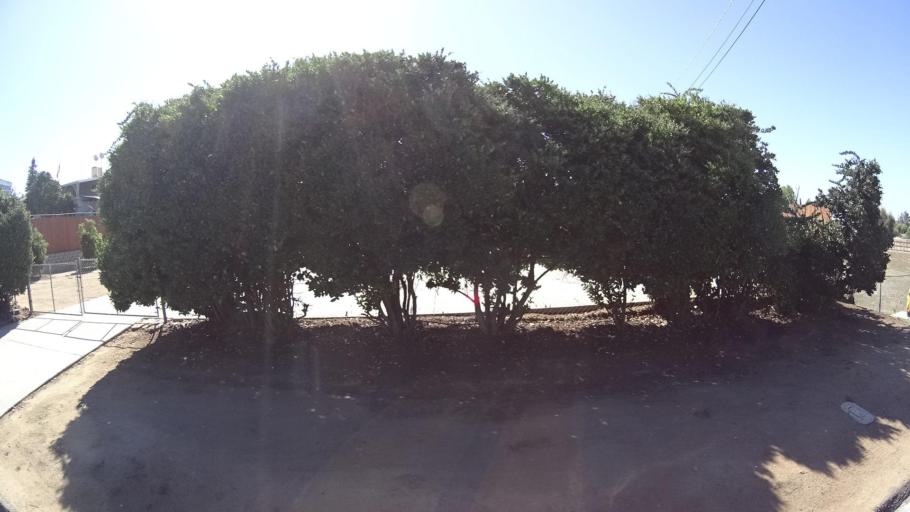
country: US
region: California
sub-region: San Diego County
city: Winter Gardens
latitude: 32.8241
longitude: -116.9230
